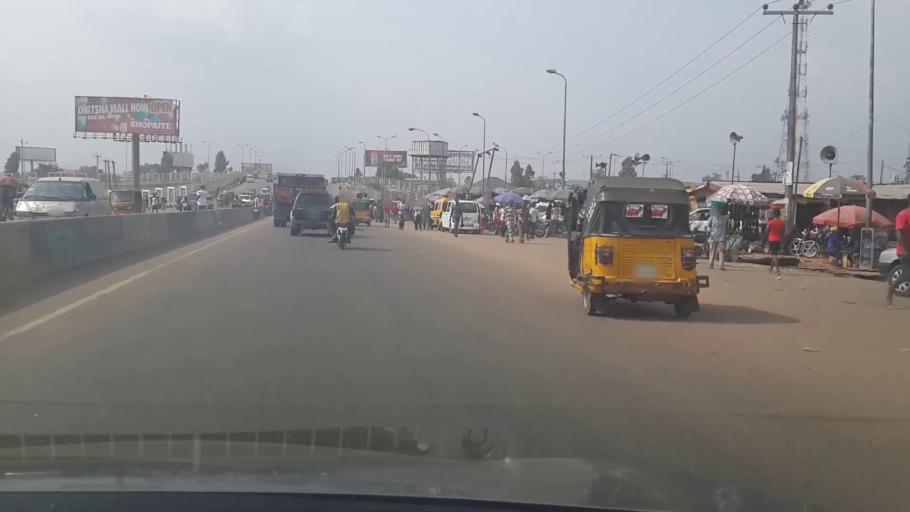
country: NG
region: Delta
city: Agbor
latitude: 6.2574
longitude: 6.1824
